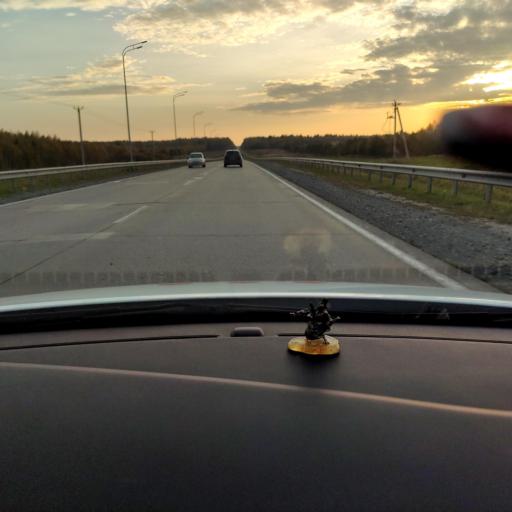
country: RU
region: Tatarstan
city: Stolbishchi
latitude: 55.6704
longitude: 49.1763
